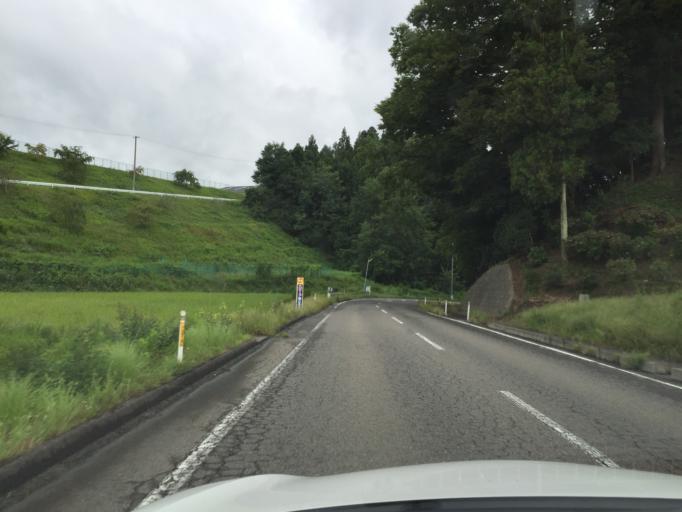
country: JP
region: Fukushima
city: Funehikimachi-funehiki
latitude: 37.4563
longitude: 140.5310
